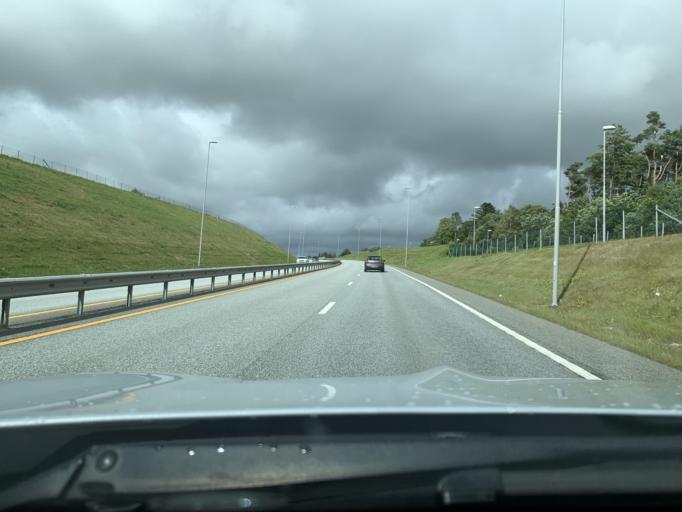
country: NO
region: Rogaland
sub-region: Sandnes
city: Sandnes
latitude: 58.8178
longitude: 5.6992
